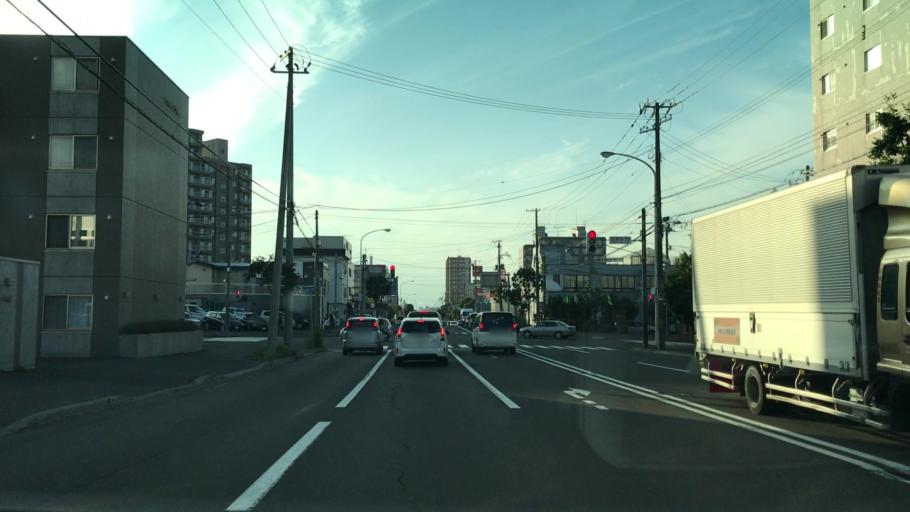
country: JP
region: Hokkaido
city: Sapporo
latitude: 43.0938
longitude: 141.2832
